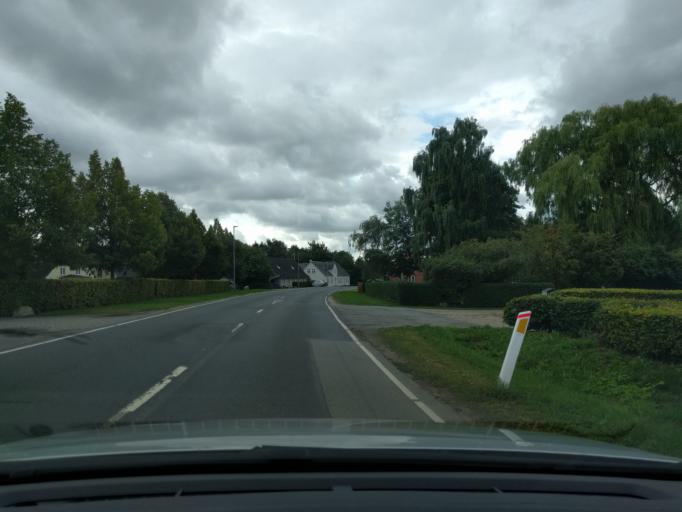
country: DK
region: South Denmark
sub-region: Nyborg Kommune
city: Ullerslev
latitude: 55.3839
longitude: 10.6675
